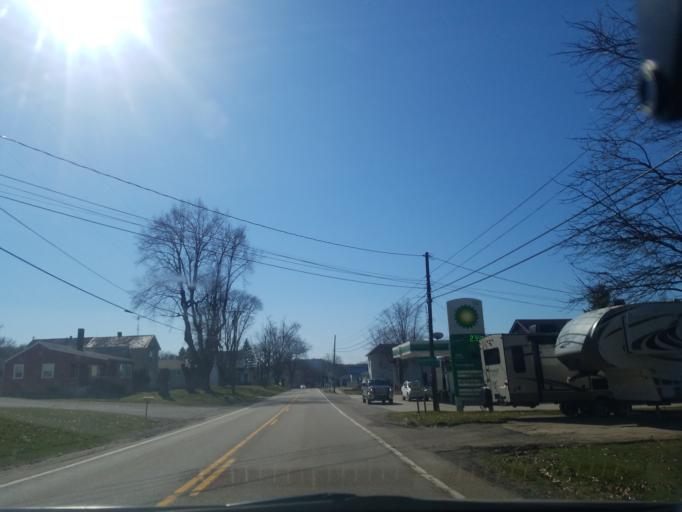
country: US
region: Ohio
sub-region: Tuscarawas County
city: Rockford
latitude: 40.5010
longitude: -81.2442
